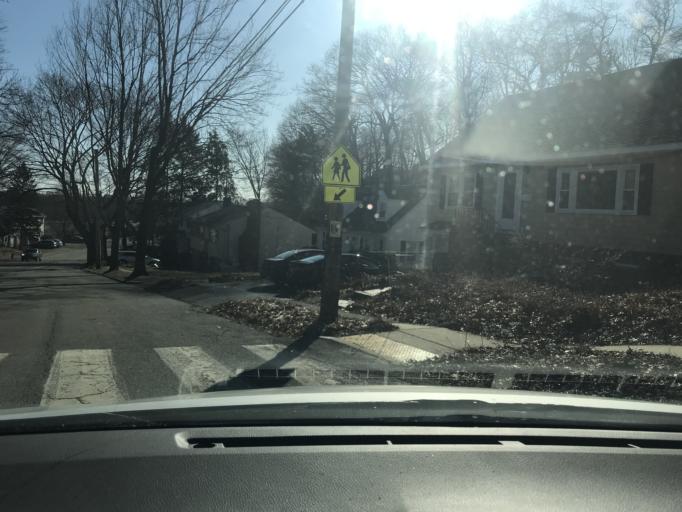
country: US
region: Massachusetts
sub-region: Middlesex County
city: Arlington
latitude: 42.4272
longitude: -71.1558
